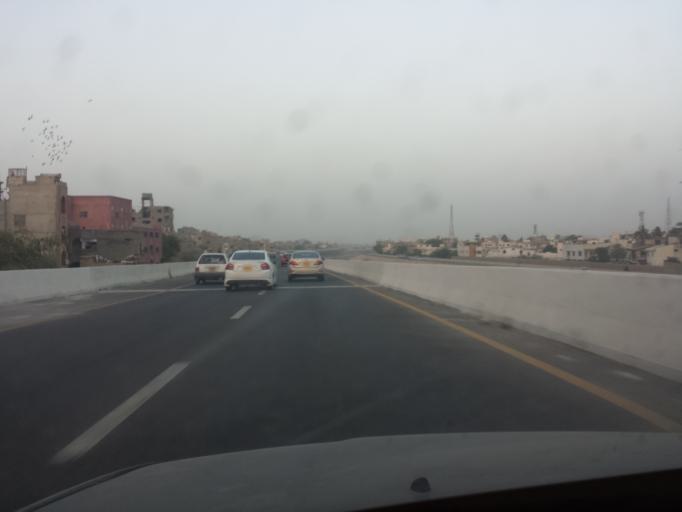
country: PK
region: Sindh
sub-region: Karachi District
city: Karachi
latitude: 24.8947
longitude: 67.0469
